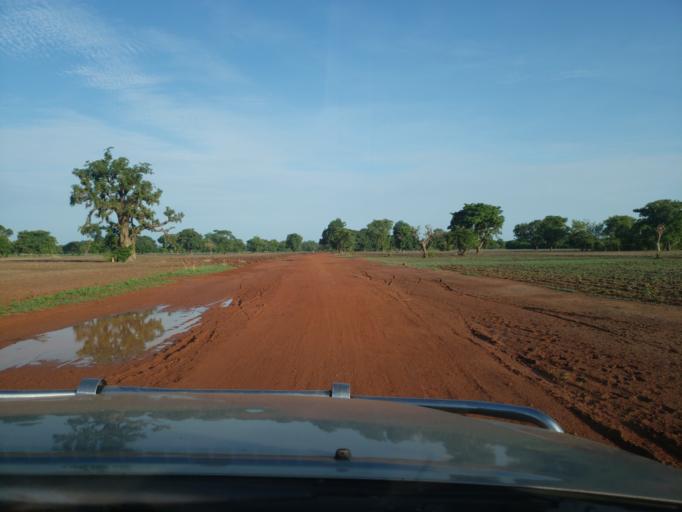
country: ML
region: Sikasso
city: Koutiala
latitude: 12.4068
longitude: -5.5450
